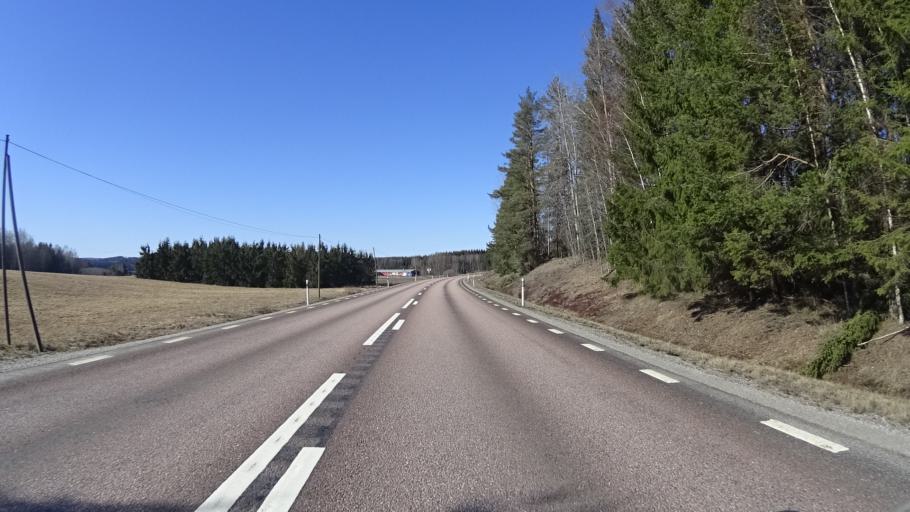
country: SE
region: Vaermland
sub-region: Sunne Kommun
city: Sunne
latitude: 59.6311
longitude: 12.9498
